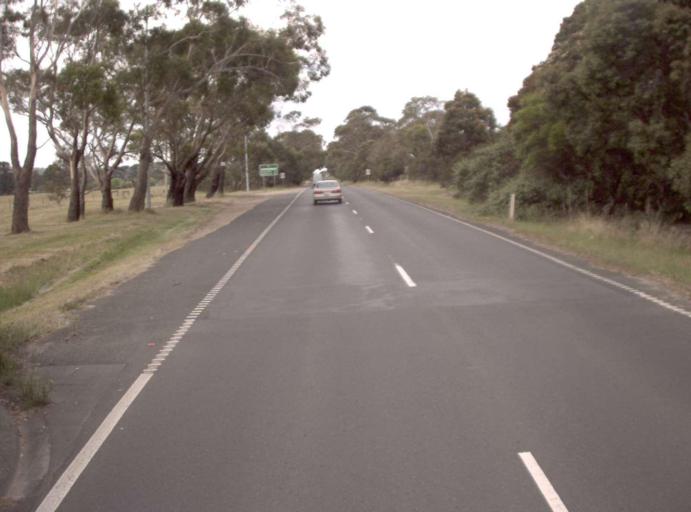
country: AU
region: Victoria
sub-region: Mornington Peninsula
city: Moorooduc
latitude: -38.2302
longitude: 145.0932
